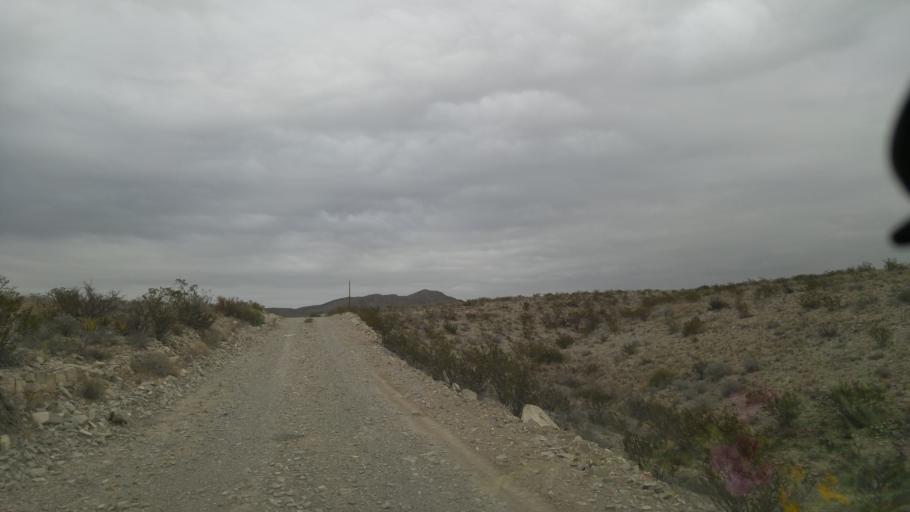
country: US
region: Texas
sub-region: Brewster County
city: Alpine
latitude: 29.5820
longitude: -103.3629
